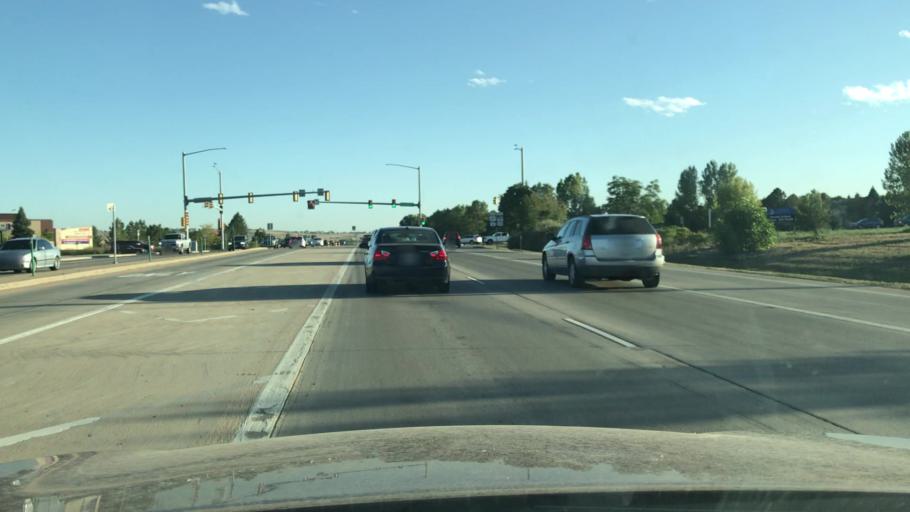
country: US
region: Colorado
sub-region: Boulder County
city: Lafayette
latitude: 39.9734
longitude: -105.0903
